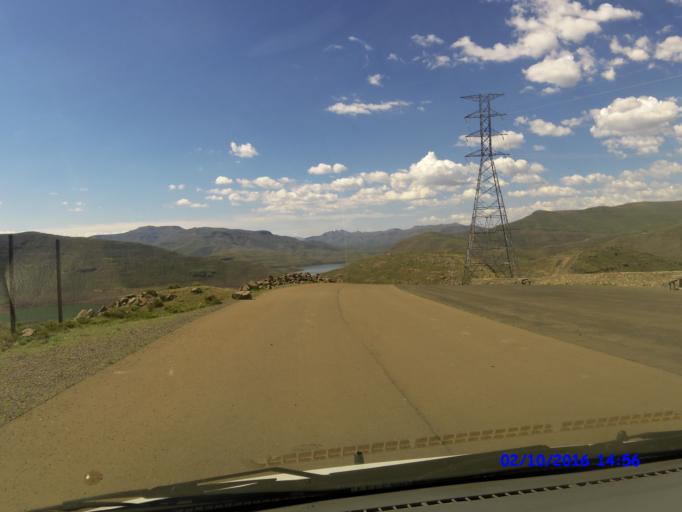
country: LS
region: Maseru
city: Nako
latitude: -29.4702
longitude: 28.0895
